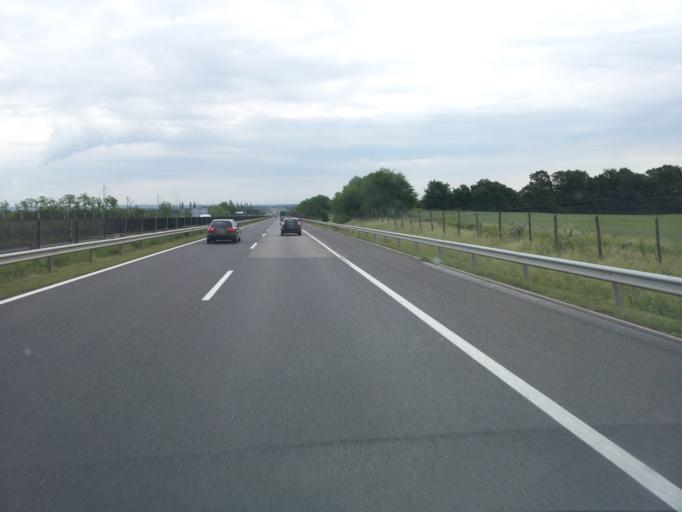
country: HU
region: Heves
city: Nagyrede
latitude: 47.7264
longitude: 19.8763
